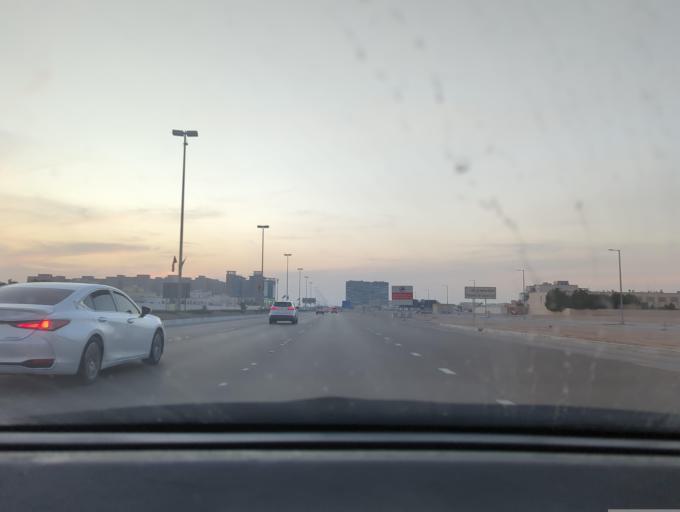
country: AE
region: Abu Dhabi
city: Abu Dhabi
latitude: 24.3748
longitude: 54.5473
